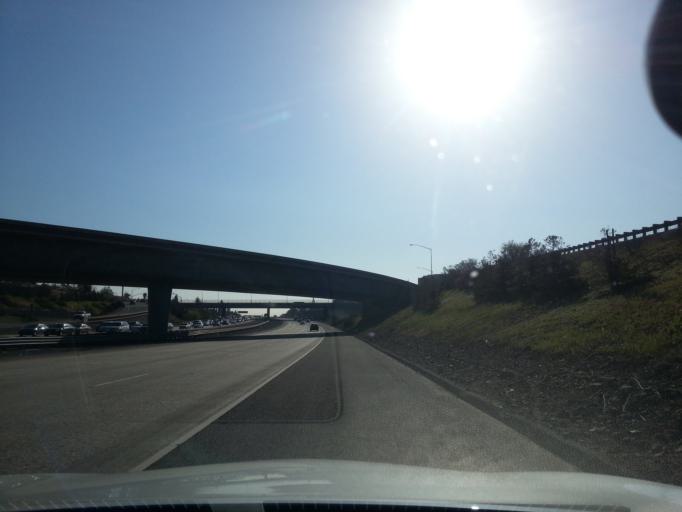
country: US
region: California
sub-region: Santa Clara County
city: Cambrian Park
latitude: 37.2553
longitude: -121.9555
